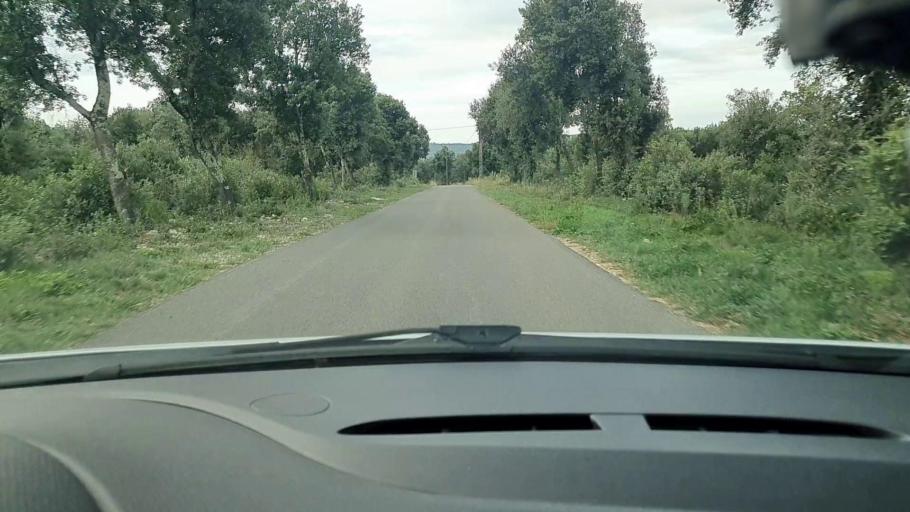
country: FR
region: Languedoc-Roussillon
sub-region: Departement du Gard
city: Mons
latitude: 44.1430
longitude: 4.2525
